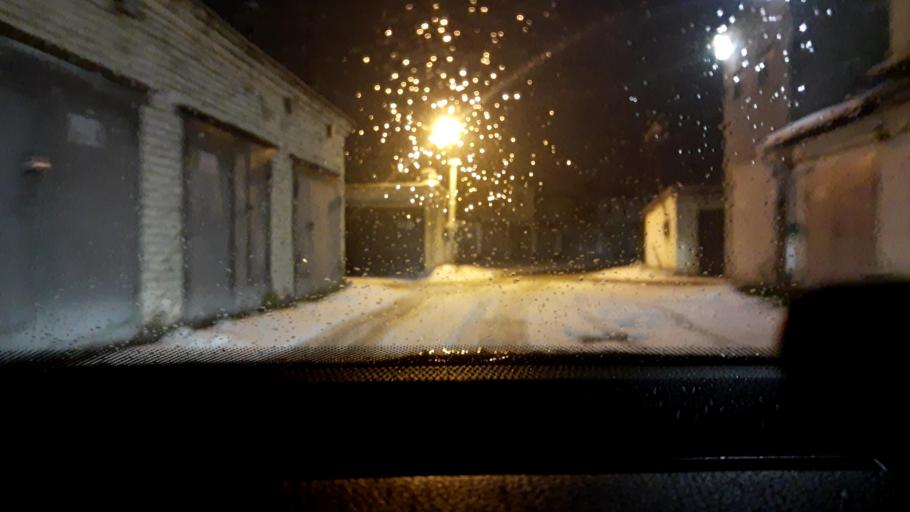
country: RU
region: Moskovskaya
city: Skhodnya
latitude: 55.9511
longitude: 37.2774
